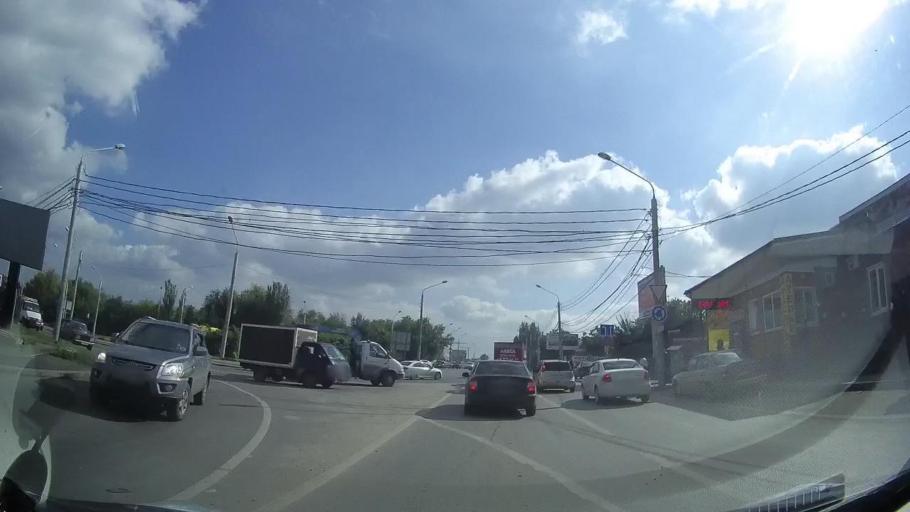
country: RU
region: Rostov
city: Severnyy
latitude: 47.2813
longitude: 39.6826
